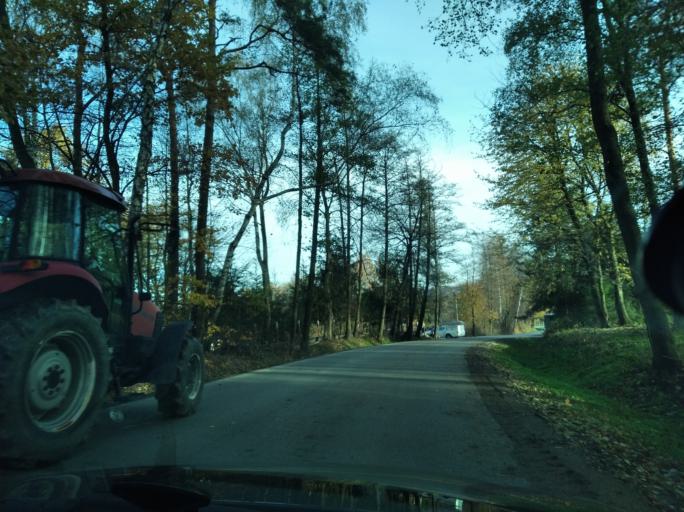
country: PL
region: Subcarpathian Voivodeship
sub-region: Powiat rzeszowski
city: Siedliska
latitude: 49.9448
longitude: 21.9792
